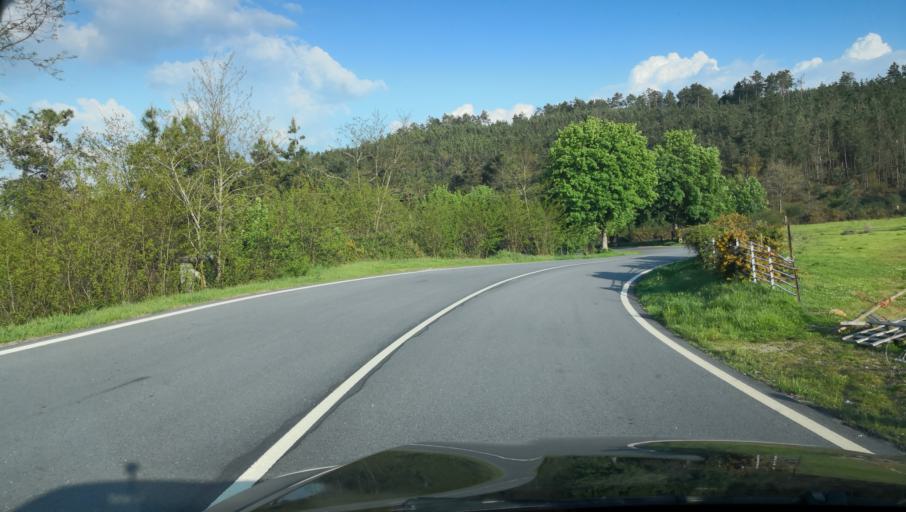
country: PT
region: Vila Real
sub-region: Santa Marta de Penaguiao
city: Santa Marta de Penaguiao
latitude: 41.2823
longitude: -7.8275
